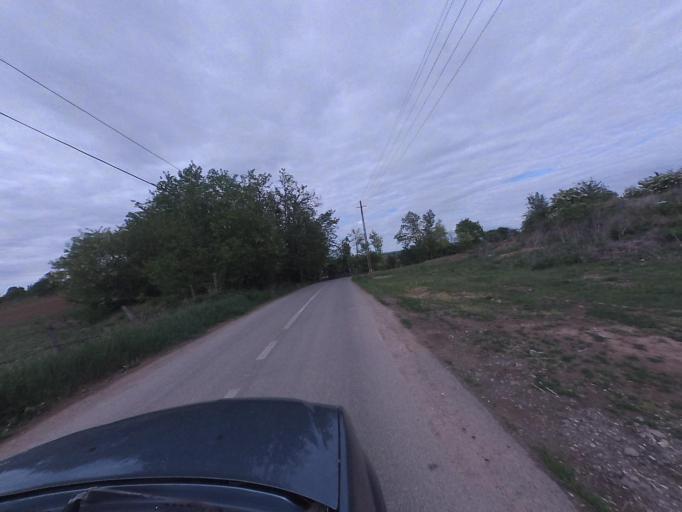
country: RO
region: Neamt
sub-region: Comuna Cordun
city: Pildesti
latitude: 46.9618
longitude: 26.8244
